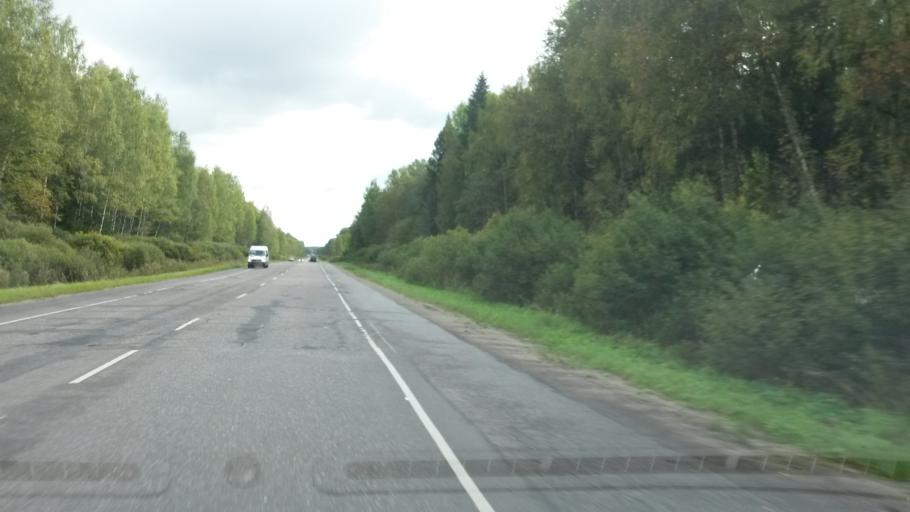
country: RU
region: Ivanovo
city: Kaminskiy
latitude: 57.0852
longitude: 41.5917
